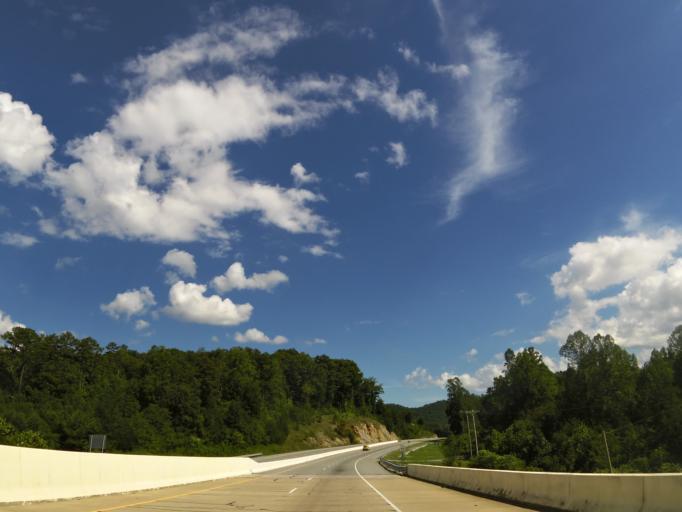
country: US
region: Tennessee
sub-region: Claiborne County
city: Tazewell
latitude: 36.4013
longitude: -83.4589
